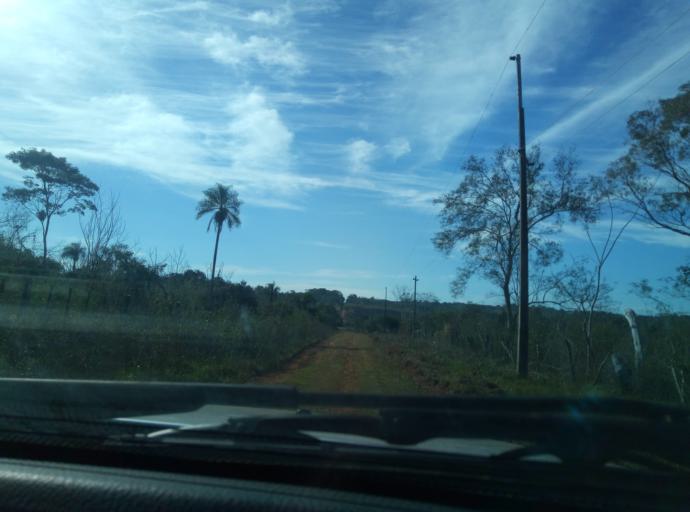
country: PY
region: Caaguazu
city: Carayao
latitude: -25.1699
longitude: -56.2932
